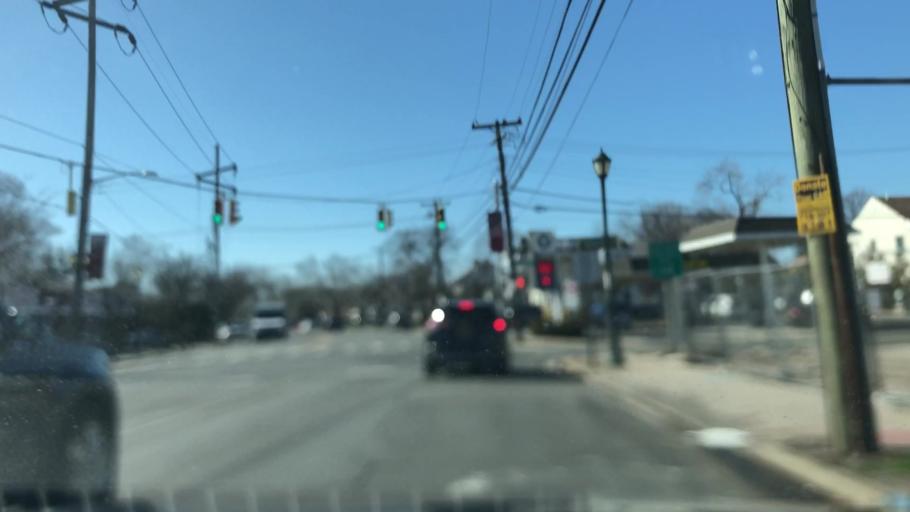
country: US
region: New York
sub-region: Nassau County
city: Malverne
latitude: 40.6882
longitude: -73.6862
